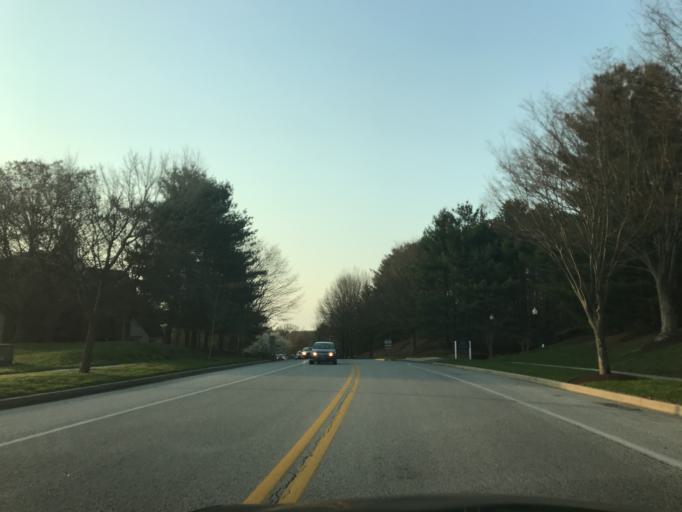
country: US
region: Maryland
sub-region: Howard County
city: Columbia
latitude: 39.2370
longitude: -76.8433
